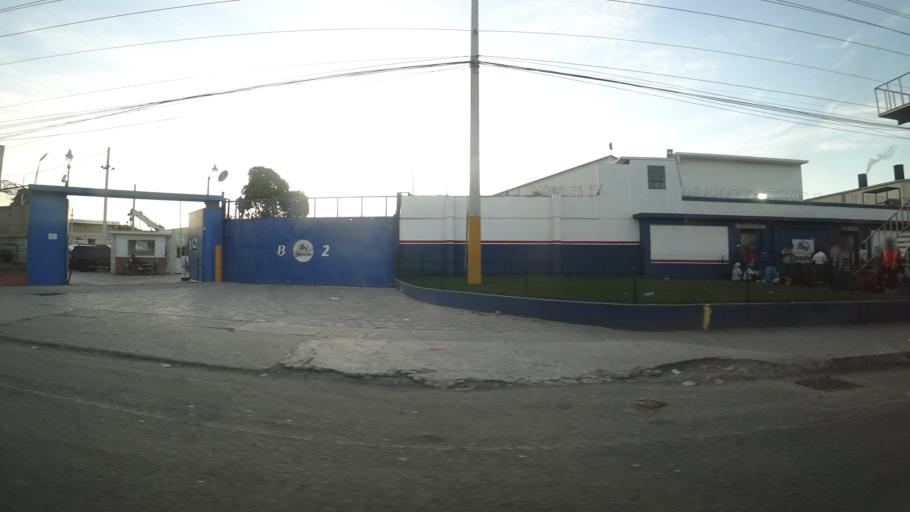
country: HT
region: Ouest
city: Delmas 73
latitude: 18.5741
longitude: -72.3052
